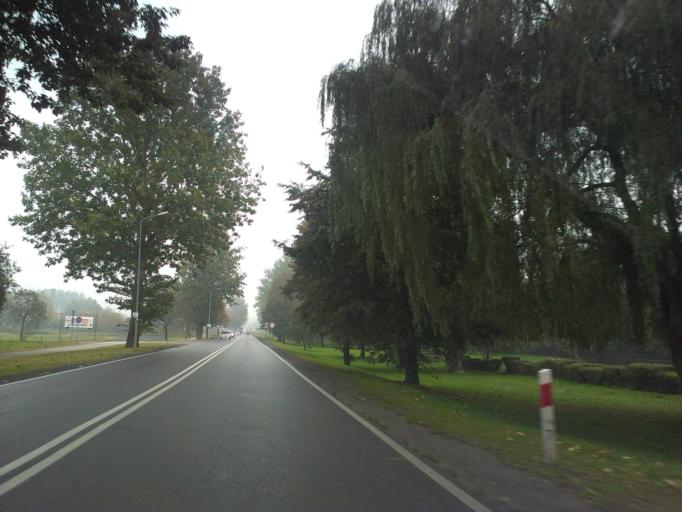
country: PL
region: West Pomeranian Voivodeship
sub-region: Powiat szczecinecki
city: Szczecinek
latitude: 53.7205
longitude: 16.6819
